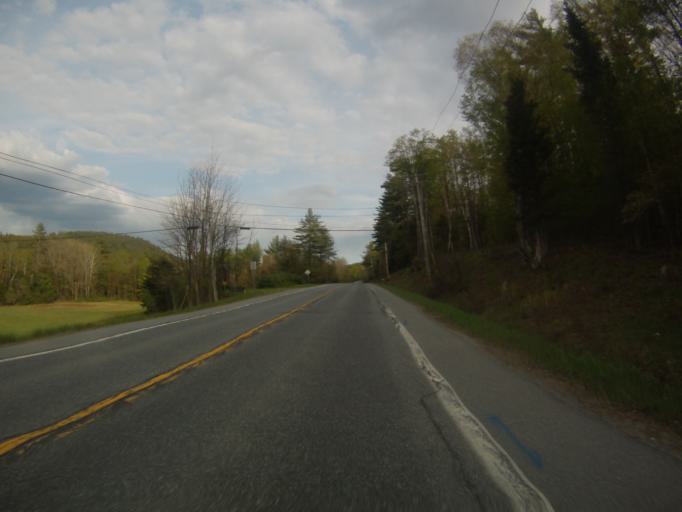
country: US
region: New York
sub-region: Warren County
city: Warrensburg
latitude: 43.6803
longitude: -73.9713
